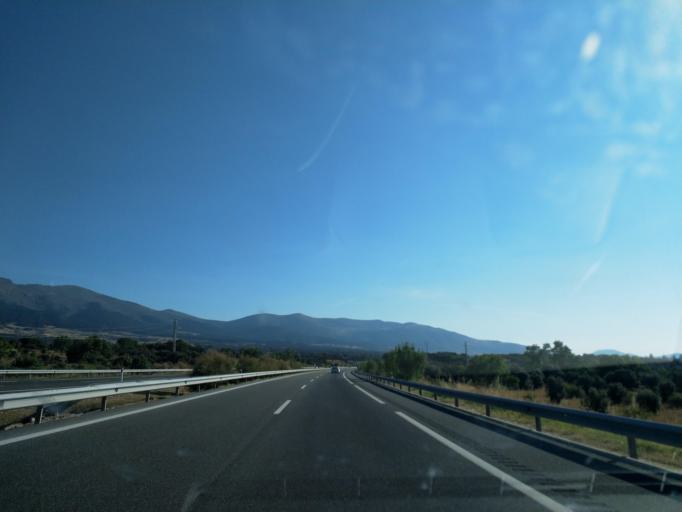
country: ES
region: Castille and Leon
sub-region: Provincia de Segovia
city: Segovia
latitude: 40.8795
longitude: -4.1186
